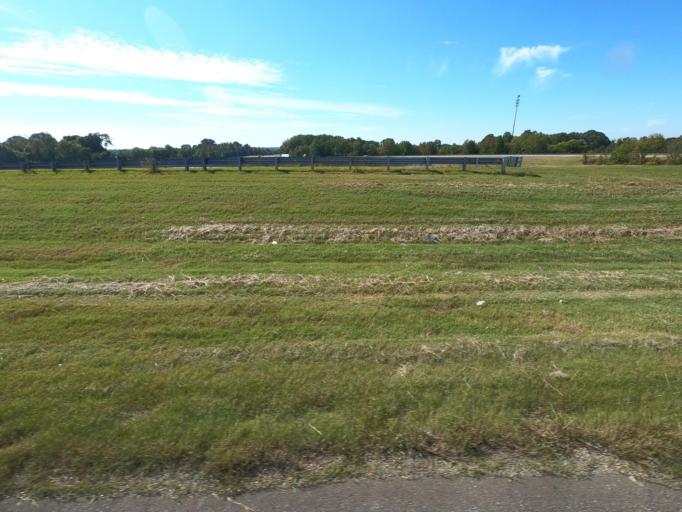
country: US
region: Tennessee
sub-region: Dyer County
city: Dyersburg
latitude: 36.0738
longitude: -89.3479
